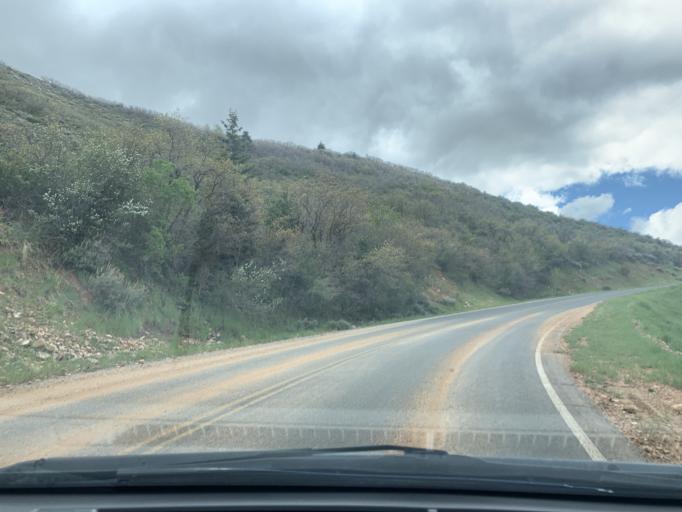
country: US
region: Utah
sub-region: Sanpete County
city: Fountain Green
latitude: 39.7879
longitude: -111.6837
